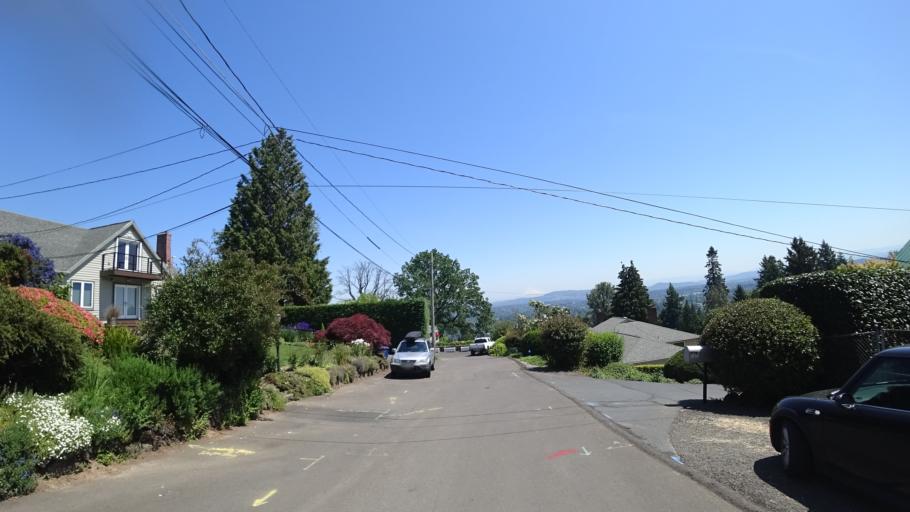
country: US
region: Oregon
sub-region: Multnomah County
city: Portland
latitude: 45.4738
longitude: -122.6810
